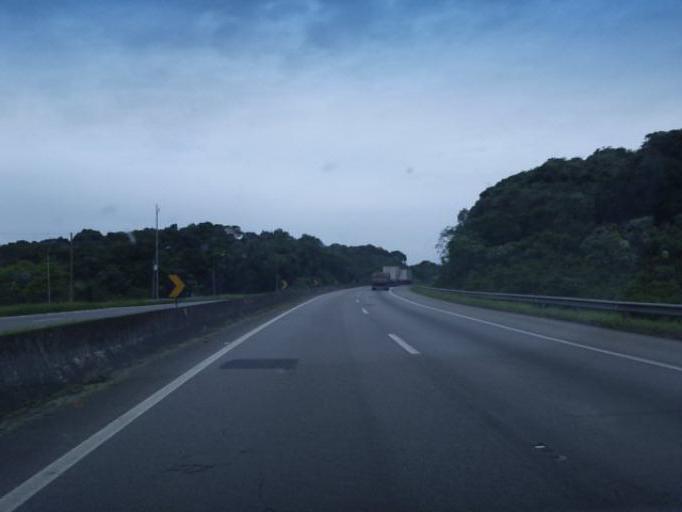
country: BR
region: Sao Paulo
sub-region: Pariquera-Acu
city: Pariquera Acu
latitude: -24.6026
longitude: -47.8765
